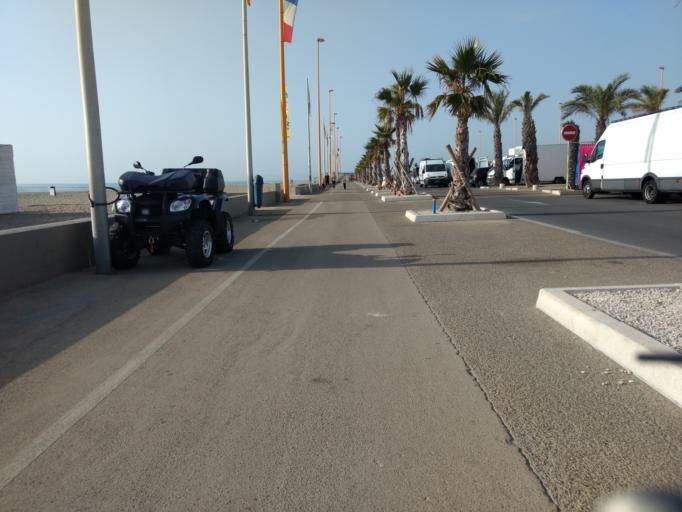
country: FR
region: Languedoc-Roussillon
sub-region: Departement des Pyrenees-Orientales
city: Le Barcares
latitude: 42.7860
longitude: 3.0384
